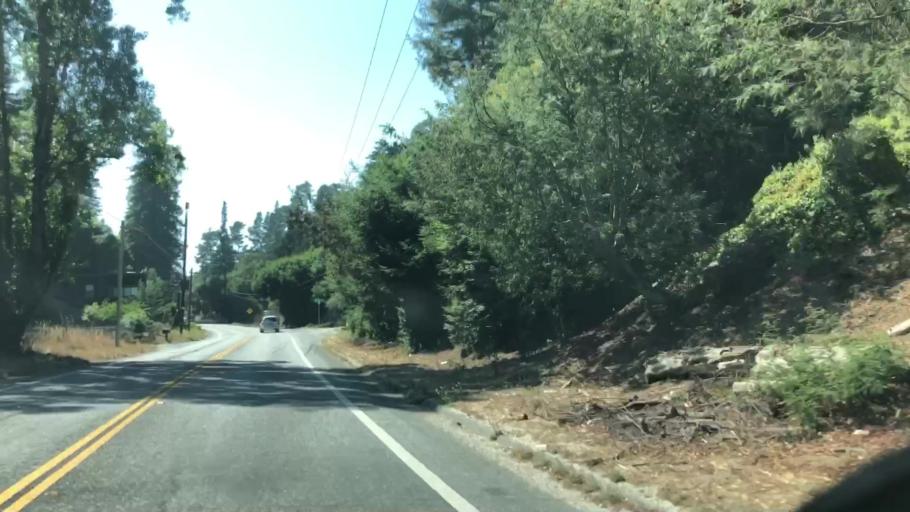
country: US
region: California
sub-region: Santa Cruz County
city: Aptos Hills-Larkin Valley
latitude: 36.9877
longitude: -121.8373
